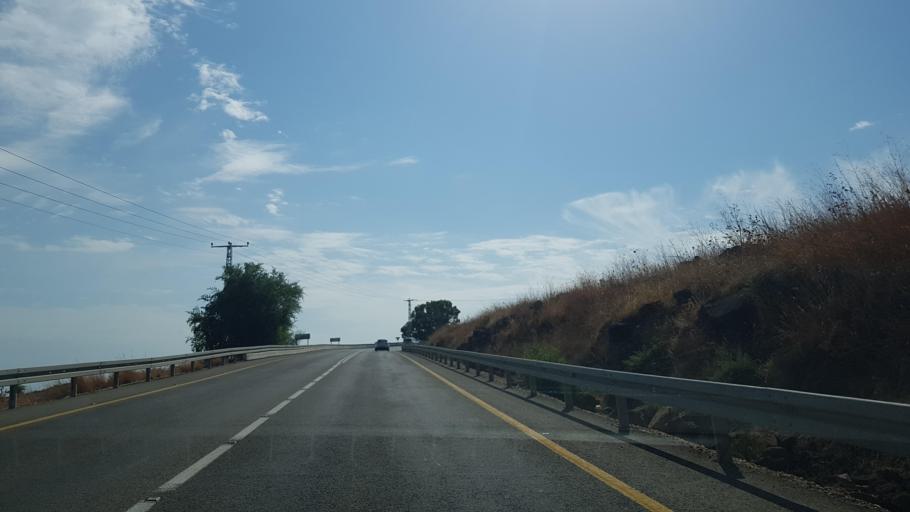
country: IL
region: Northern District
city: Rosh Pinna
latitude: 32.9079
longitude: 35.5595
